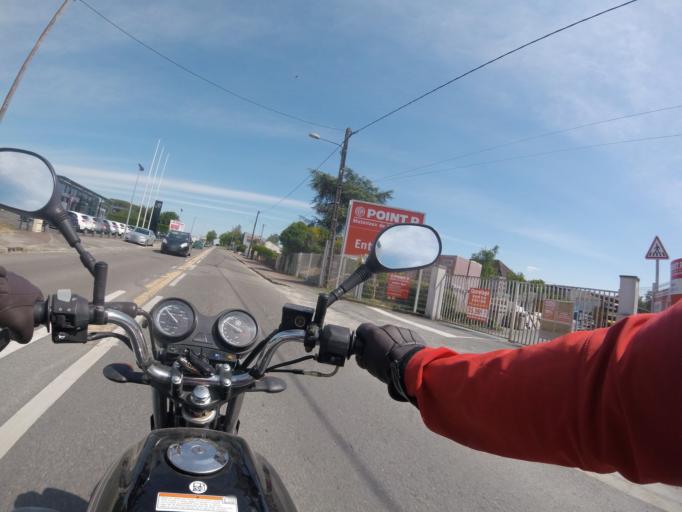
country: FR
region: Poitou-Charentes
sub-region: Departement de la Charente
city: Saint-Brice
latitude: 45.6868
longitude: -0.3086
